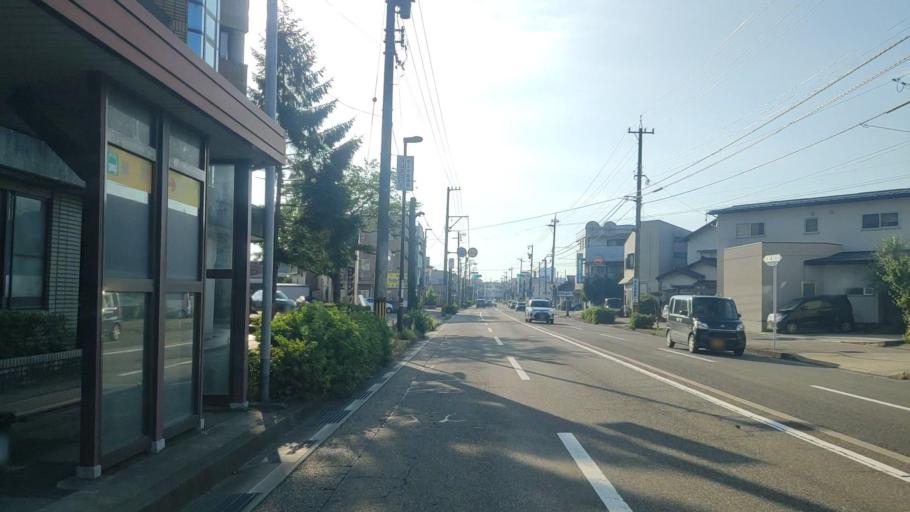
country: JP
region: Ishikawa
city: Kanazawa-shi
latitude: 36.5616
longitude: 136.6757
